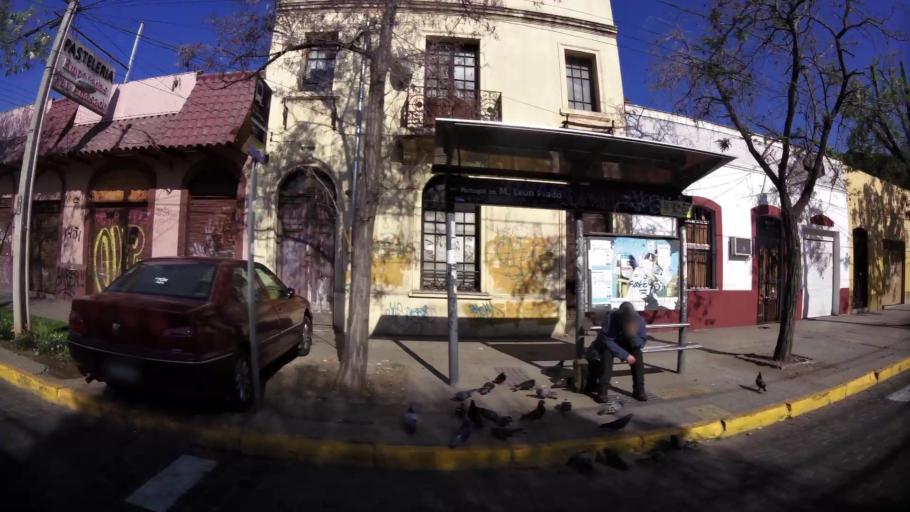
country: CL
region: Santiago Metropolitan
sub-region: Provincia de Santiago
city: Santiago
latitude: -33.4623
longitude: -70.6318
